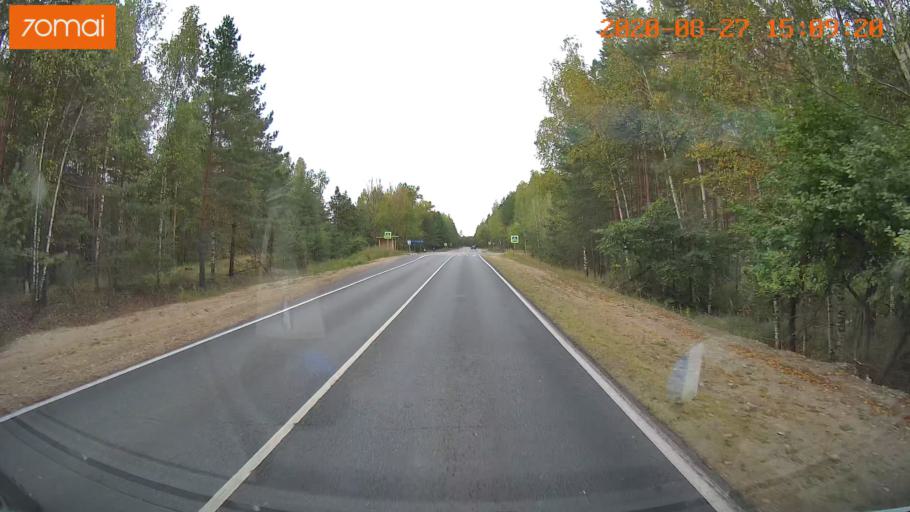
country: RU
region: Vladimir
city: Kurlovo
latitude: 55.5036
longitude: 40.5719
